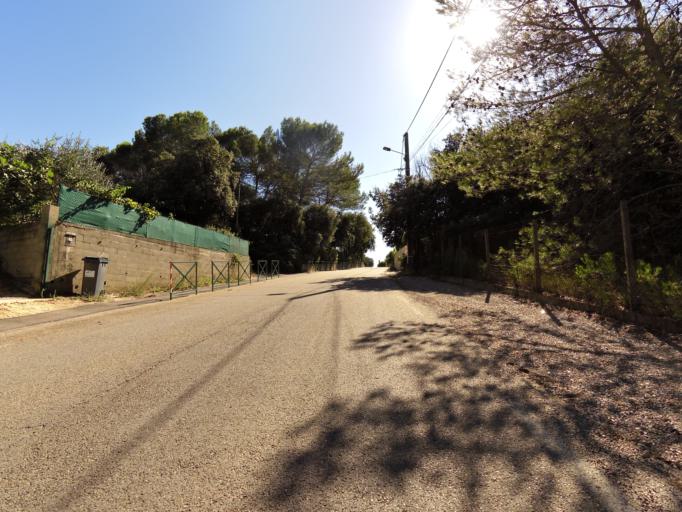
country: FR
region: Languedoc-Roussillon
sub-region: Departement du Gard
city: Mus
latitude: 43.7425
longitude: 4.2042
